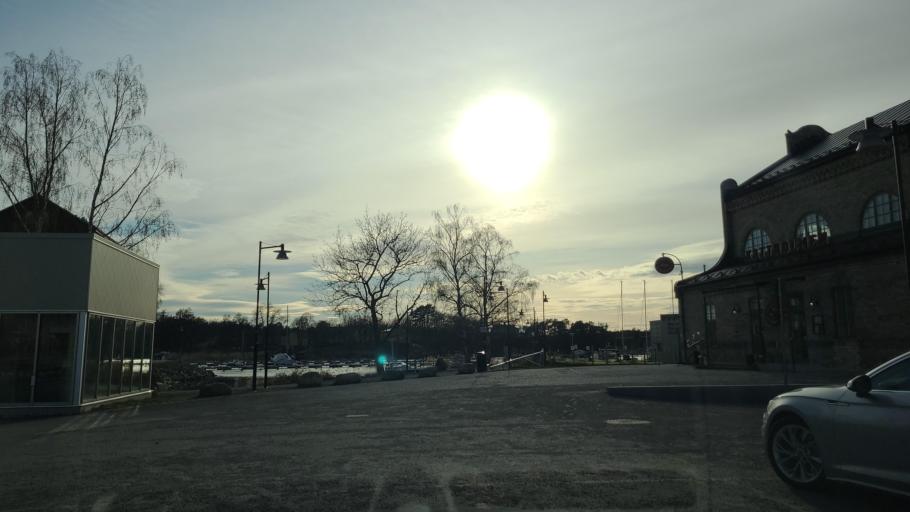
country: SE
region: Stockholm
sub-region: Varmdo Kommun
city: Gustavsberg
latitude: 59.3241
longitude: 18.3782
